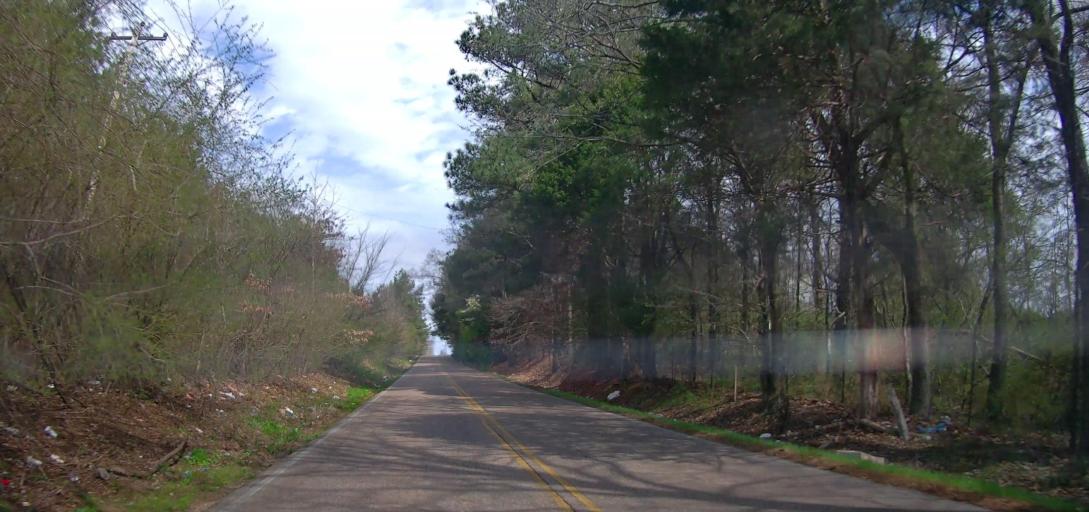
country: US
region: Mississippi
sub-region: De Soto County
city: Olive Branch
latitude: 34.9969
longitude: -89.8484
